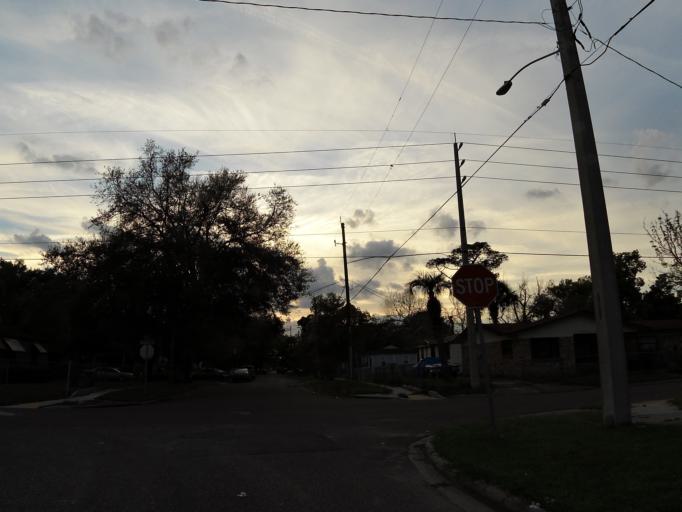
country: US
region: Florida
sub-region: Duval County
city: Jacksonville
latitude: 30.3590
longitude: -81.6305
